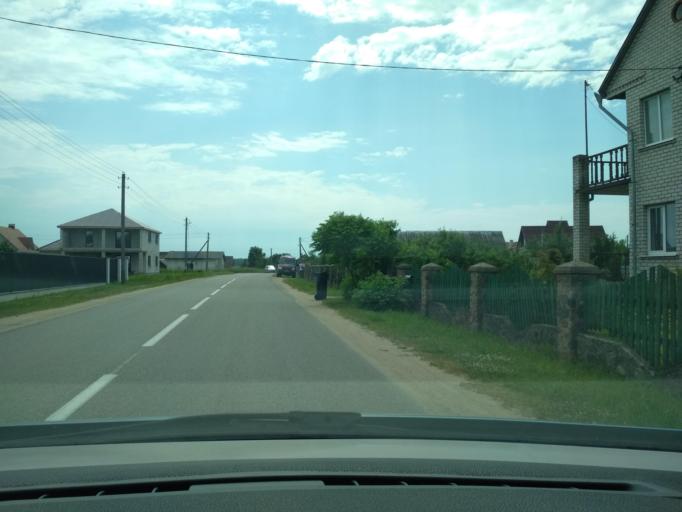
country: BY
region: Grodnenskaya
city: Astravyets
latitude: 54.6039
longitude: 25.9605
